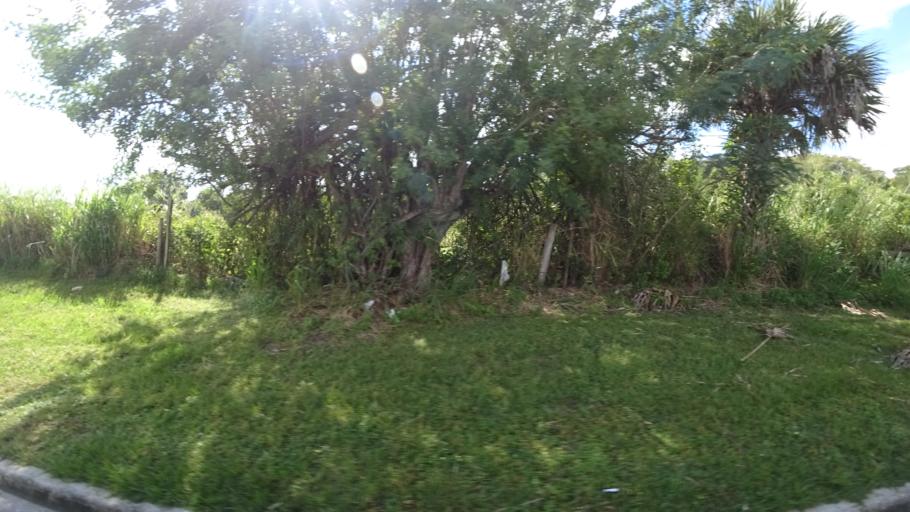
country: US
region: Florida
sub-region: Manatee County
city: Samoset
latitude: 27.4878
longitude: -82.5327
